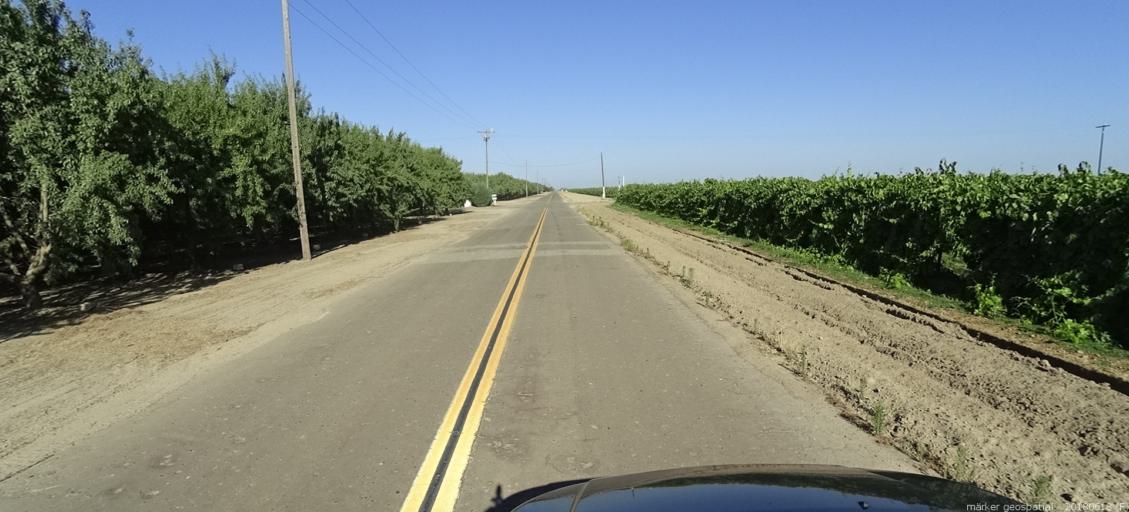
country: US
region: California
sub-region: Fresno County
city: Biola
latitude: 36.8223
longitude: -120.1049
